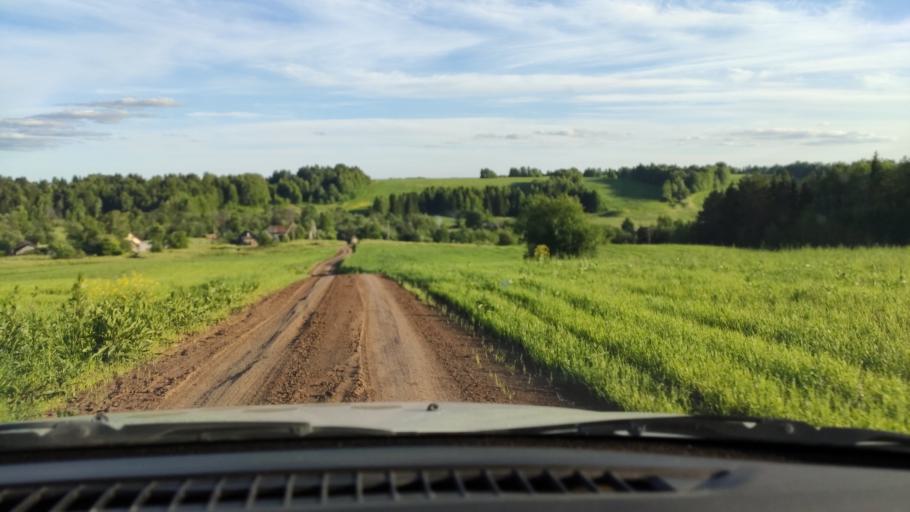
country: RU
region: Perm
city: Orda
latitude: 57.2940
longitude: 56.5942
